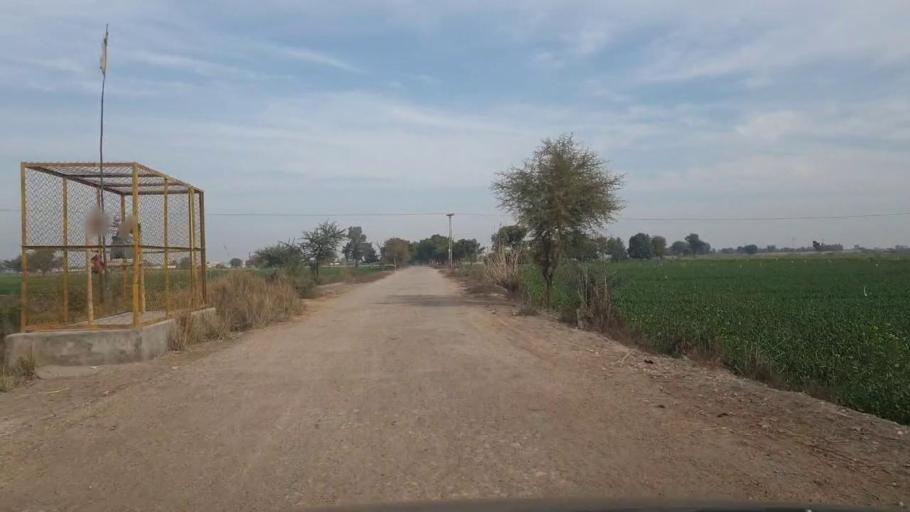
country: PK
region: Sindh
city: Khadro
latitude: 26.1530
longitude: 68.6948
